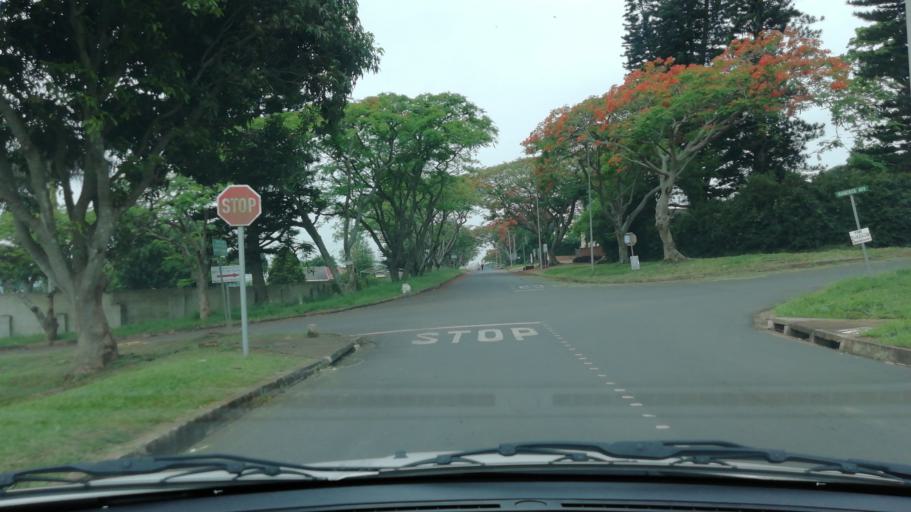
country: ZA
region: KwaZulu-Natal
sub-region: uThungulu District Municipality
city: Empangeni
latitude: -28.7396
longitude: 31.8884
